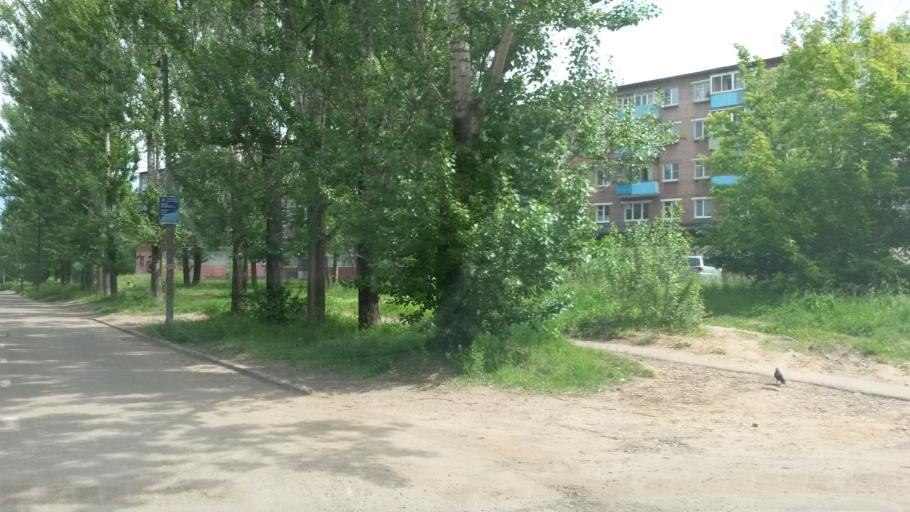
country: RU
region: Jaroslavl
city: Yaroslavl
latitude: 57.5879
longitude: 39.8285
